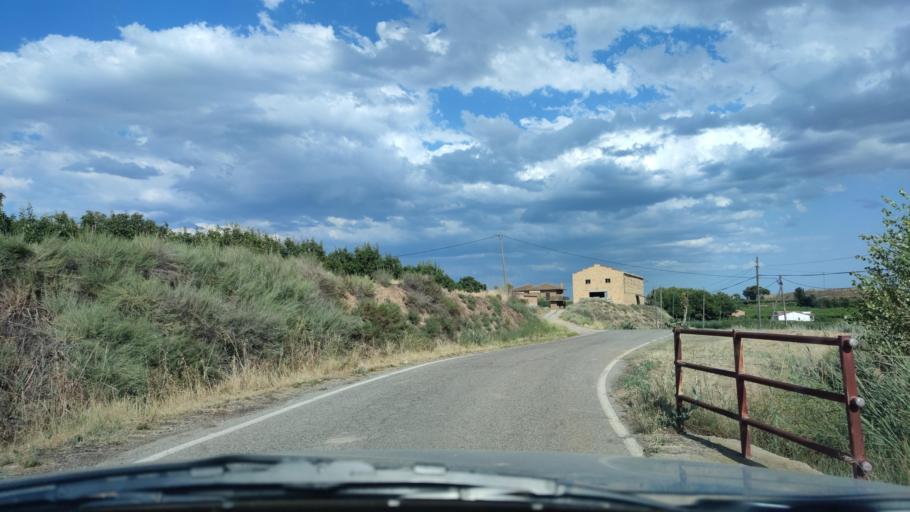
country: ES
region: Catalonia
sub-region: Provincia de Lleida
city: Alpicat
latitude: 41.6299
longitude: 0.5674
